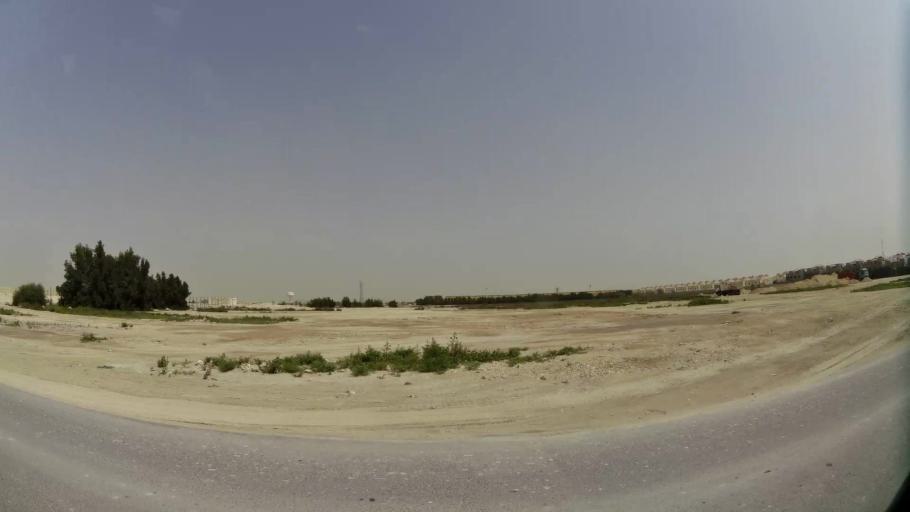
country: QA
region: Baladiyat ar Rayyan
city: Ar Rayyan
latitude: 25.2327
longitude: 51.4074
